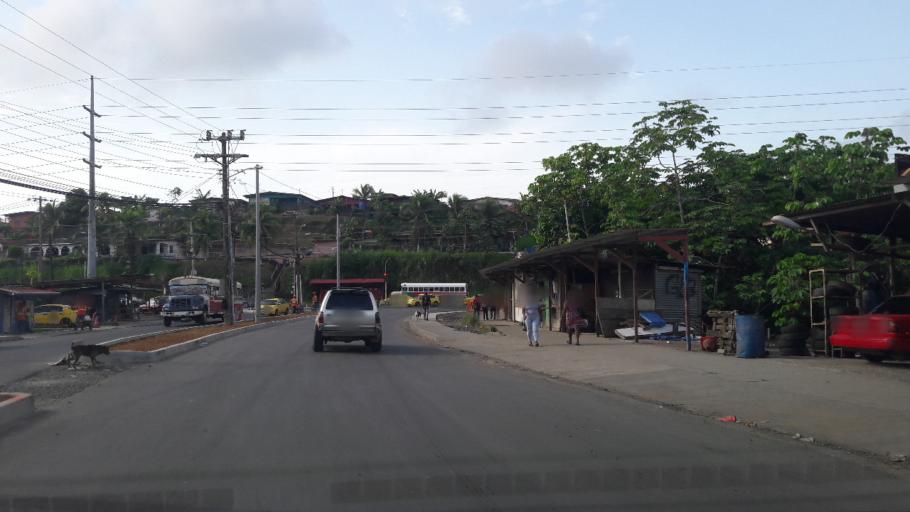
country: PA
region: Colon
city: Cativa
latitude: 9.3548
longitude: -79.8507
